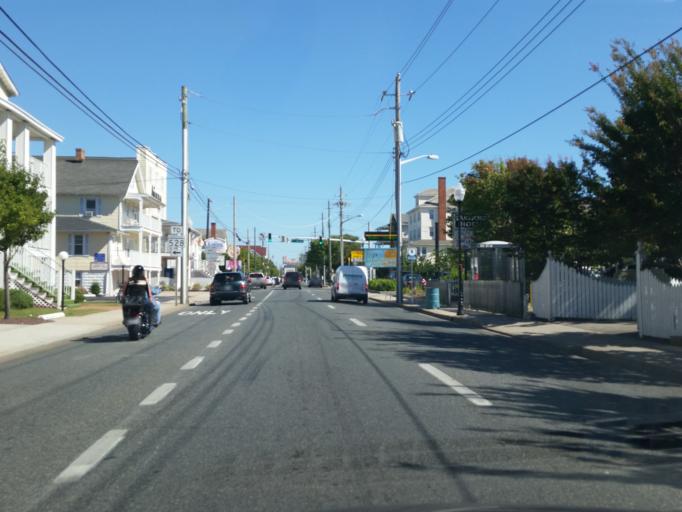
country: US
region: Maryland
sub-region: Worcester County
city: Ocean City
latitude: 38.3391
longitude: -75.0822
